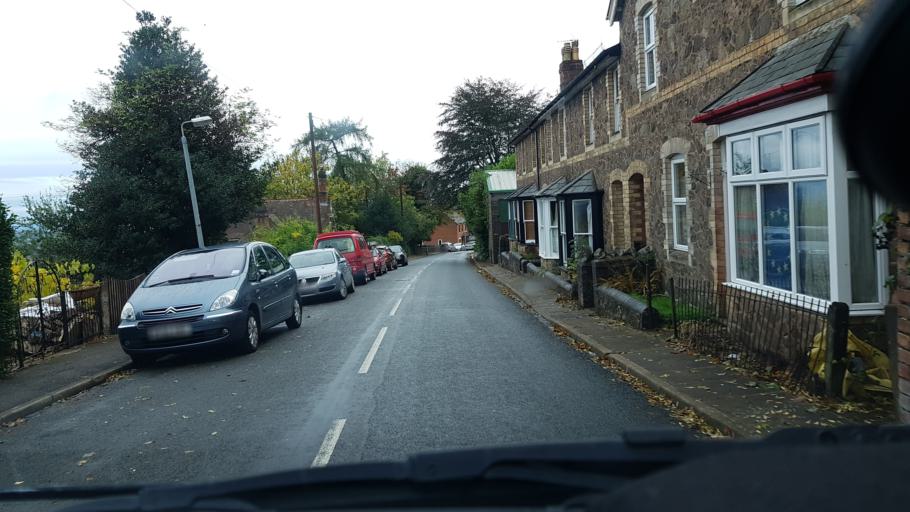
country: GB
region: England
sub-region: Worcestershire
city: Great Malvern
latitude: 52.1234
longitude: -2.3406
